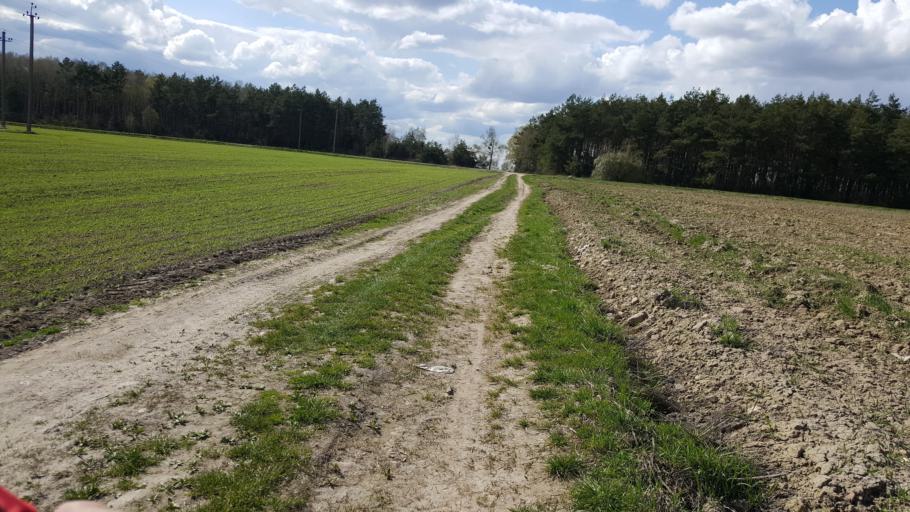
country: BY
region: Brest
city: Kamyanyets
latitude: 52.3911
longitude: 23.6424
